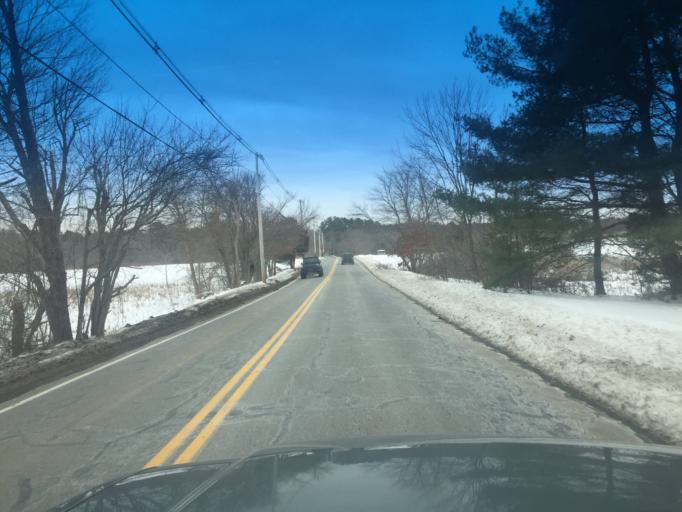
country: US
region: Massachusetts
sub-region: Norfolk County
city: Norfolk
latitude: 42.1201
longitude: -71.3003
